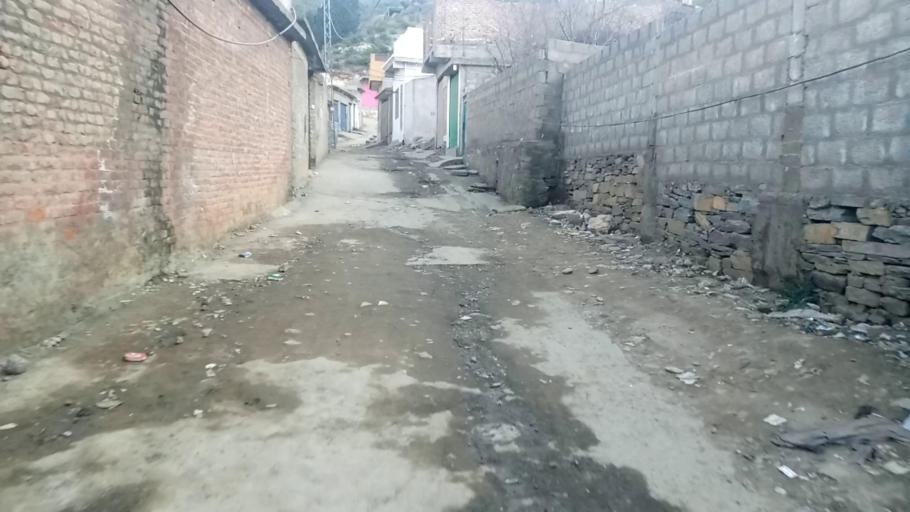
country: PK
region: Khyber Pakhtunkhwa
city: Saidu Sharif
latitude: 34.7377
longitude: 72.3523
